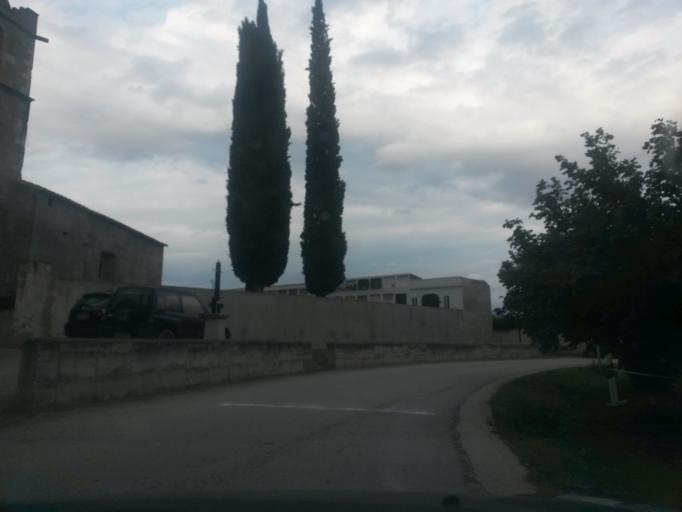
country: ES
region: Catalonia
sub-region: Provincia de Girona
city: Sant Gregori
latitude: 41.9756
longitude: 2.7031
